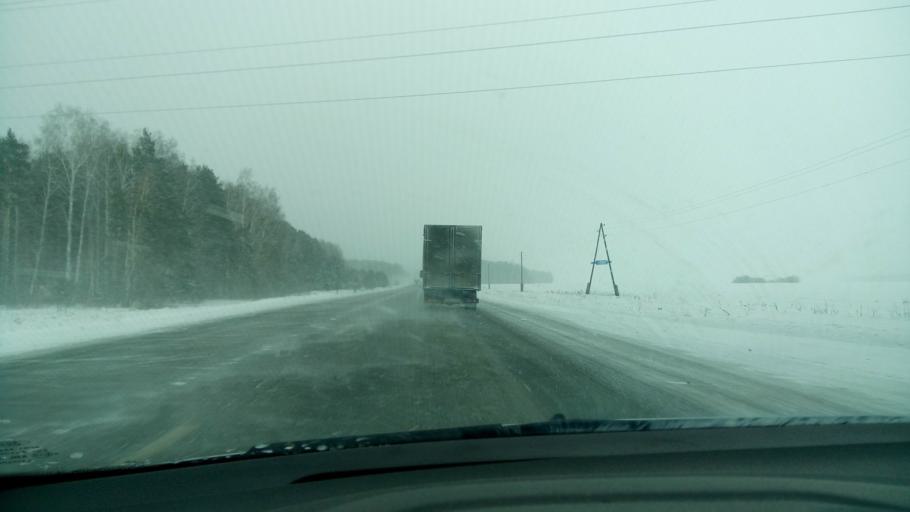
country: RU
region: Sverdlovsk
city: Gryaznovskoye
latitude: 56.7813
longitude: 61.6166
